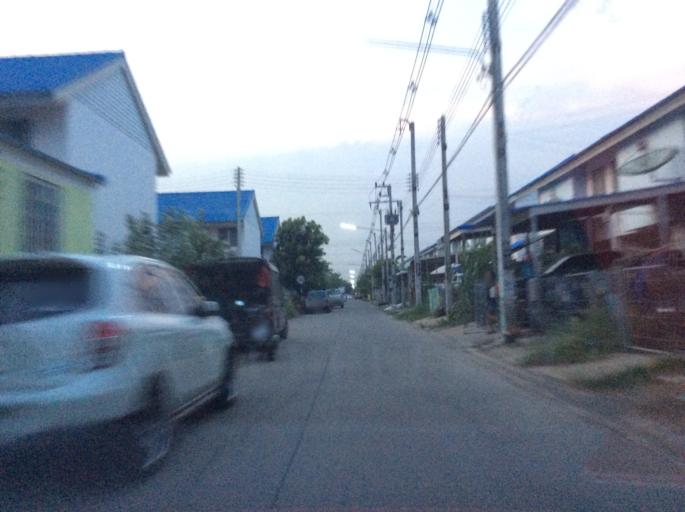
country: TH
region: Pathum Thani
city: Ban Rangsit
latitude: 14.0427
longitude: 100.7627
